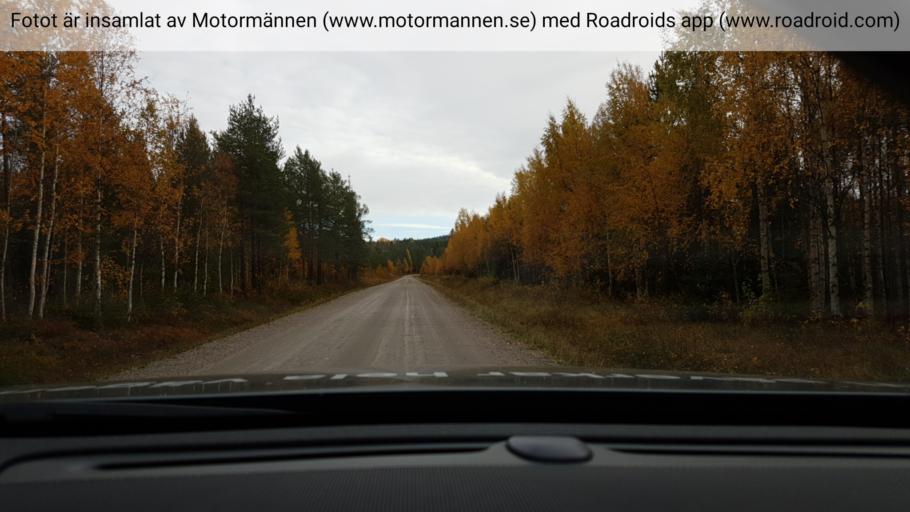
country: SE
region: Norrbotten
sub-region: Overkalix Kommun
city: OEverkalix
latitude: 66.2900
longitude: 22.9632
